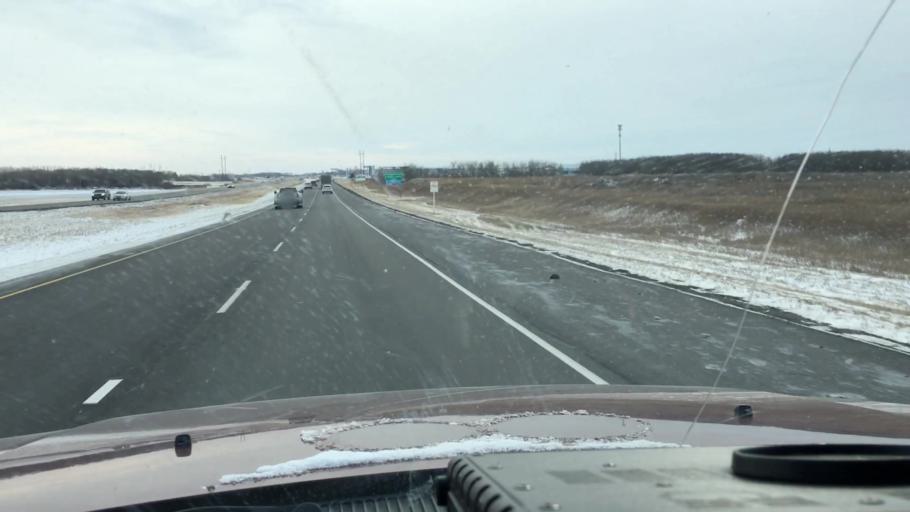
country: CA
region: Saskatchewan
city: Saskatoon
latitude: 52.0668
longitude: -106.6026
